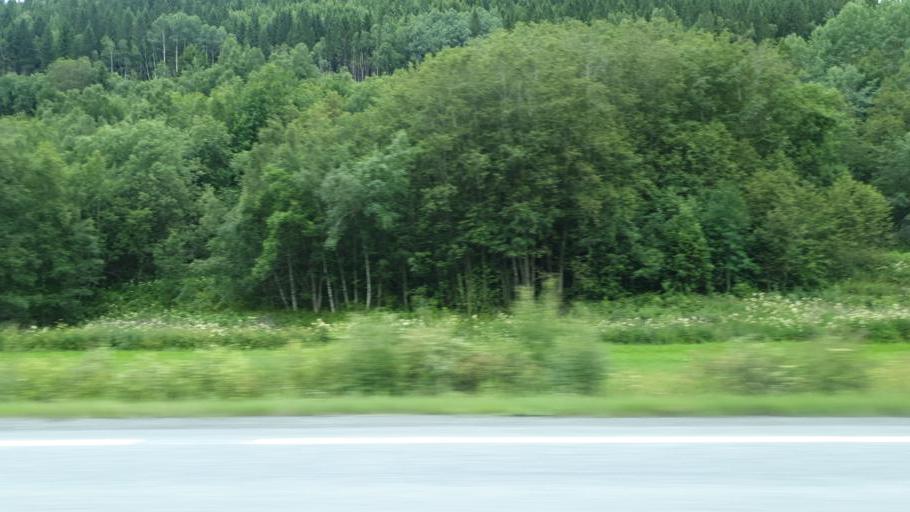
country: NO
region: Sor-Trondelag
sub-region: Midtre Gauldal
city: Storen
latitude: 63.0098
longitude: 10.2437
